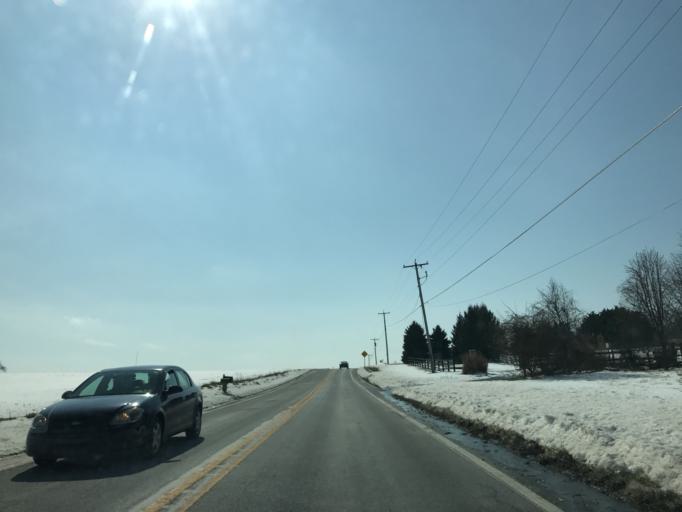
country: US
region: Pennsylvania
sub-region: York County
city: Stewartstown
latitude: 39.7019
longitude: -76.5233
